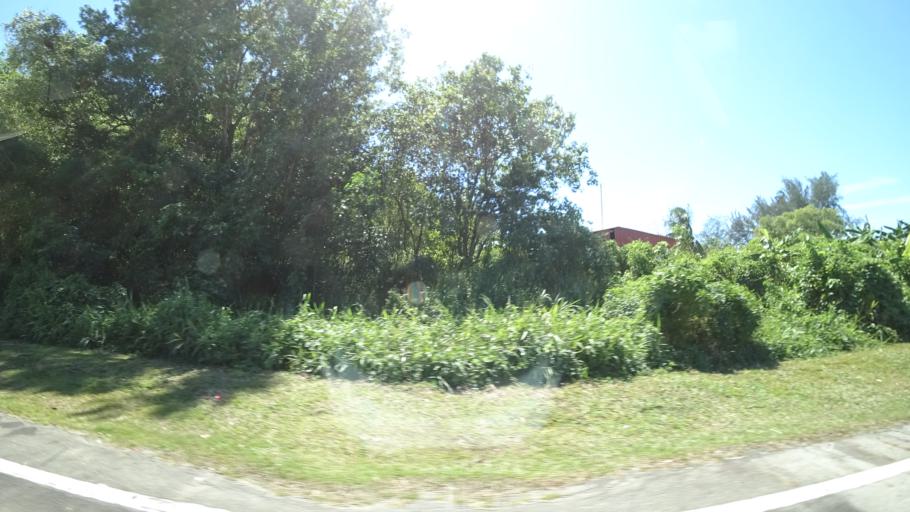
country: BN
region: Brunei and Muara
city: Bandar Seri Begawan
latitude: 4.8985
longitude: 114.9108
